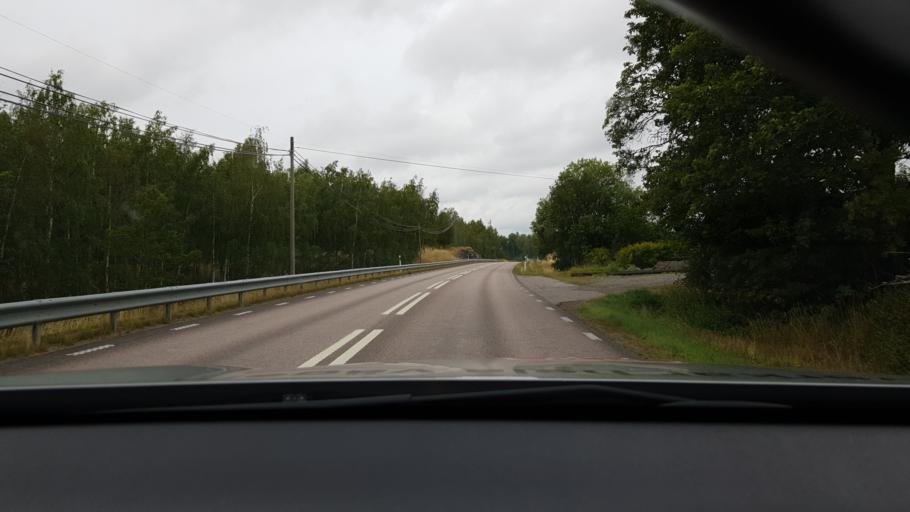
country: SE
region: Soedermanland
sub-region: Gnesta Kommun
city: Gnesta
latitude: 59.0541
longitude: 17.2452
